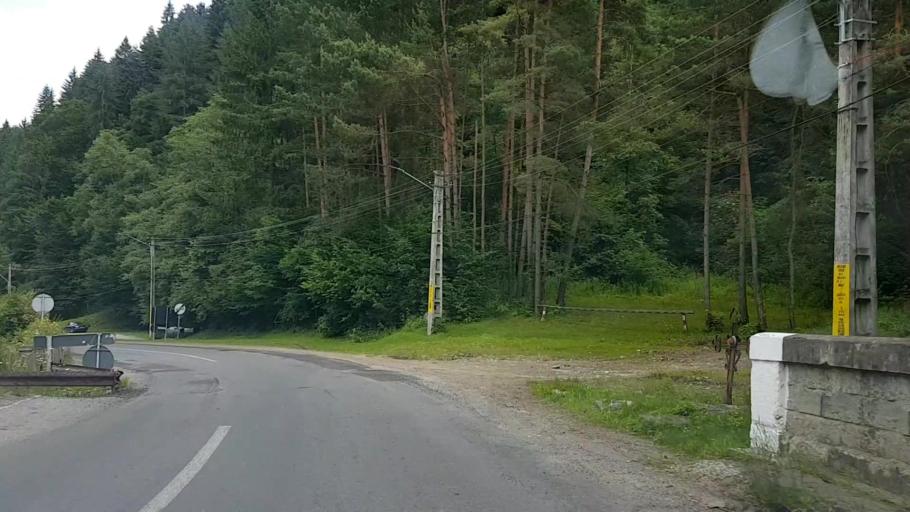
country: RO
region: Neamt
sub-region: Comuna Bicaz
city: Dodeni
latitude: 46.9383
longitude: 26.0835
